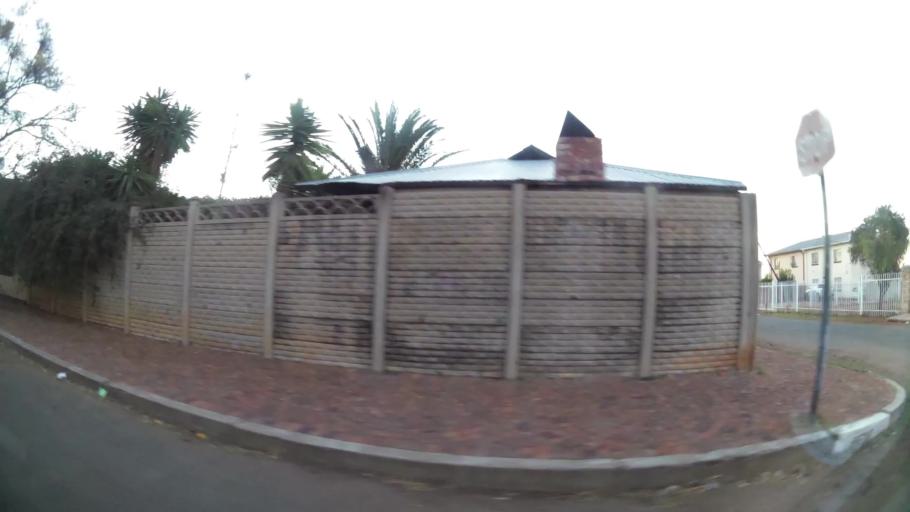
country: ZA
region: Northern Cape
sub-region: Frances Baard District Municipality
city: Kimberley
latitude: -28.7250
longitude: 24.7682
